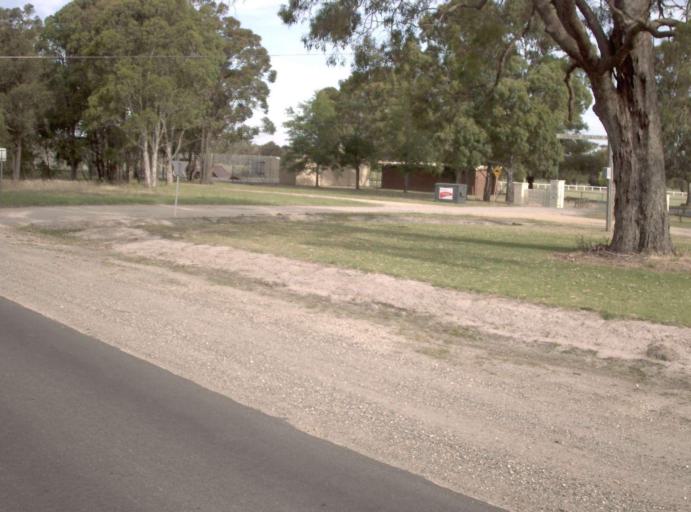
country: AU
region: Victoria
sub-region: Latrobe
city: Traralgon
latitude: -38.0599
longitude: 146.6298
